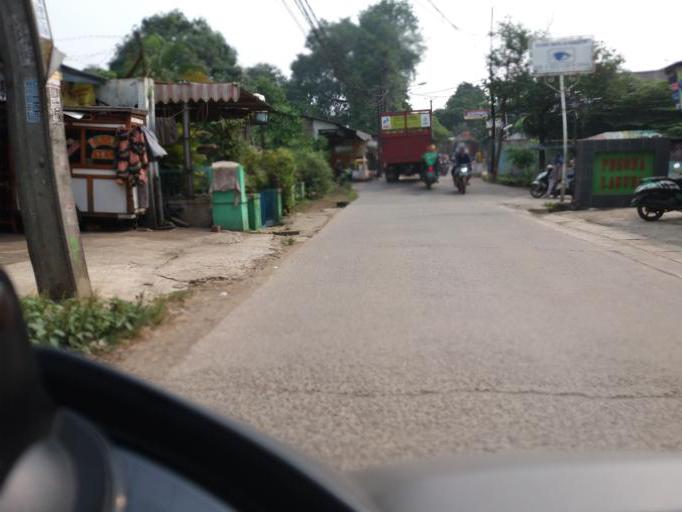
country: ID
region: West Java
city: Cibinong
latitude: -6.4444
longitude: 106.8598
